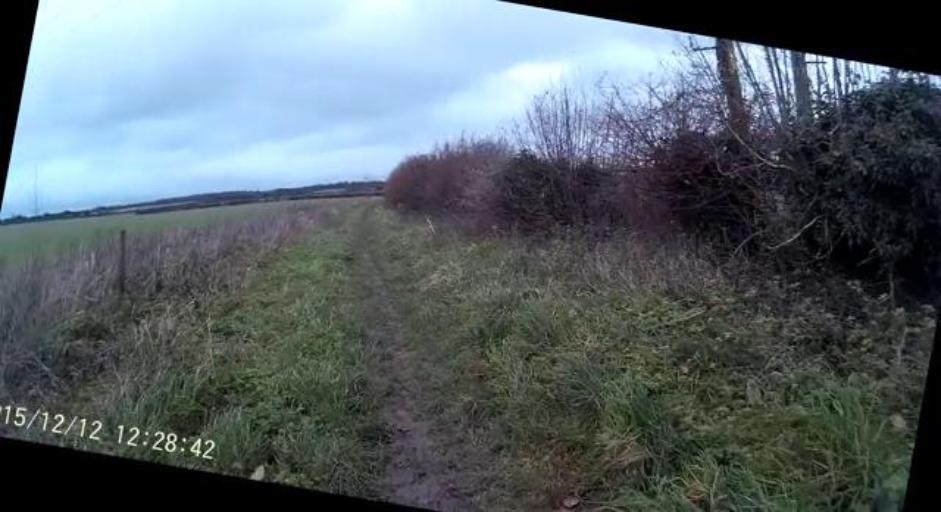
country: GB
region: England
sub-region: Hampshire
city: Cowplain
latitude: 50.9451
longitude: -0.9941
